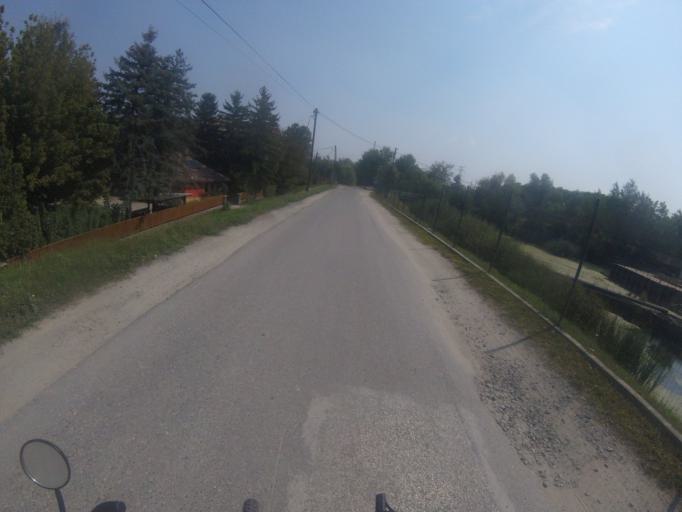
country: HU
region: Bacs-Kiskun
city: Baja
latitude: 46.1938
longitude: 18.9329
